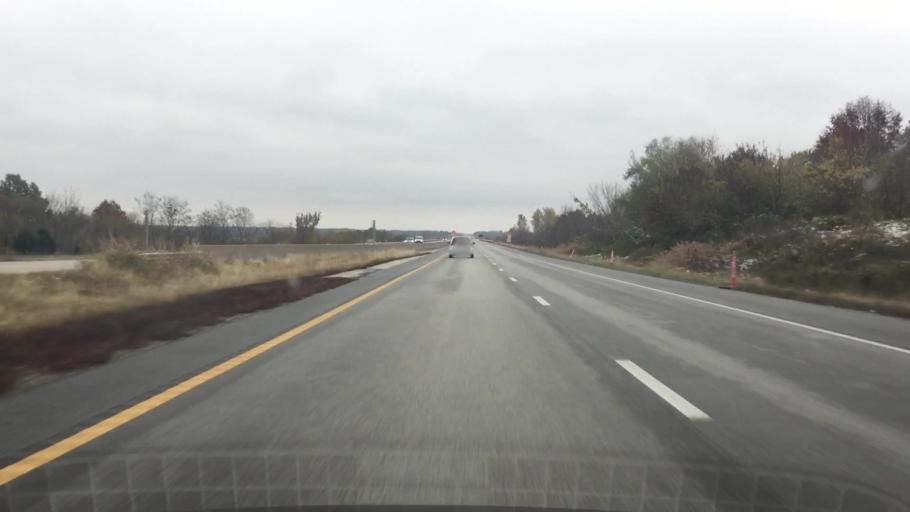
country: US
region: Missouri
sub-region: Henry County
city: Clinton
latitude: 38.2944
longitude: -93.7592
